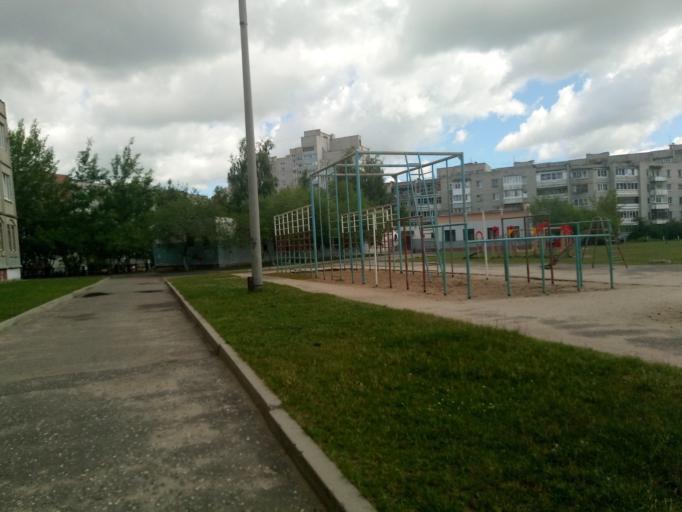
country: RU
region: Jaroslavl
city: Yaroslavl
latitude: 57.6421
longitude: 39.9538
